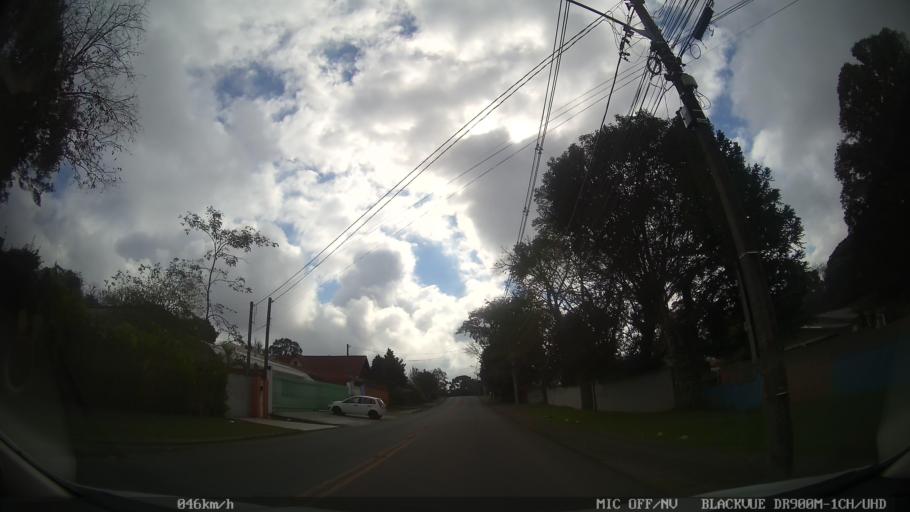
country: BR
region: Parana
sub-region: Curitiba
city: Curitiba
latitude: -25.3618
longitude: -49.2484
